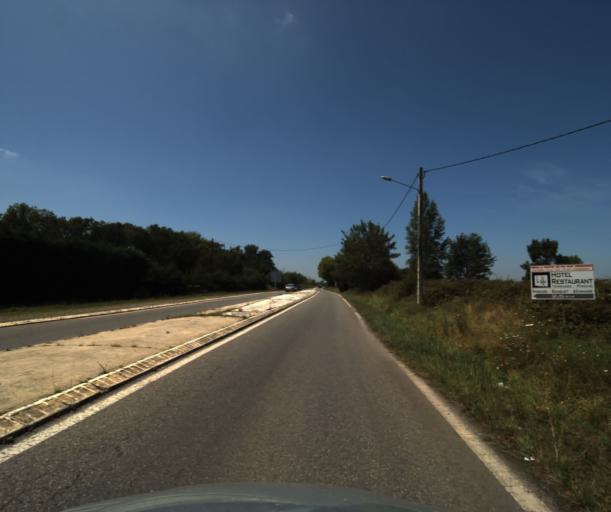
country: FR
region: Midi-Pyrenees
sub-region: Departement de la Haute-Garonne
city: Seysses
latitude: 43.4643
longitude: 1.2986
